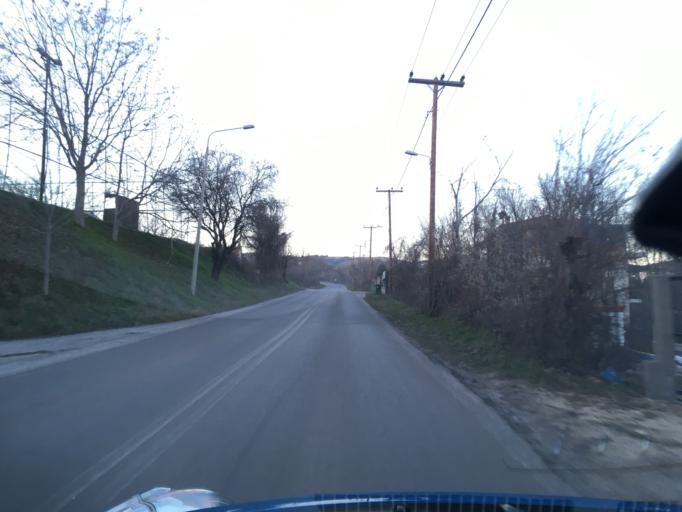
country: GR
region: West Macedonia
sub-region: Nomos Kozanis
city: Kozani
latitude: 40.2819
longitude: 21.7823
